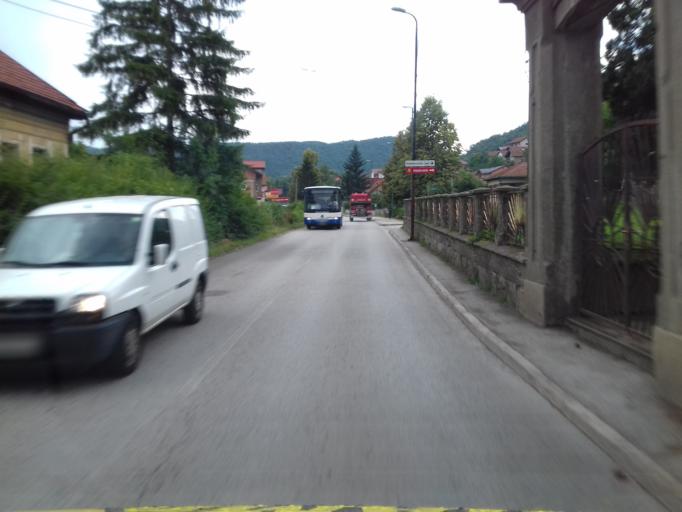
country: BA
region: Federation of Bosnia and Herzegovina
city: Visoko
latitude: 43.9820
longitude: 18.1829
